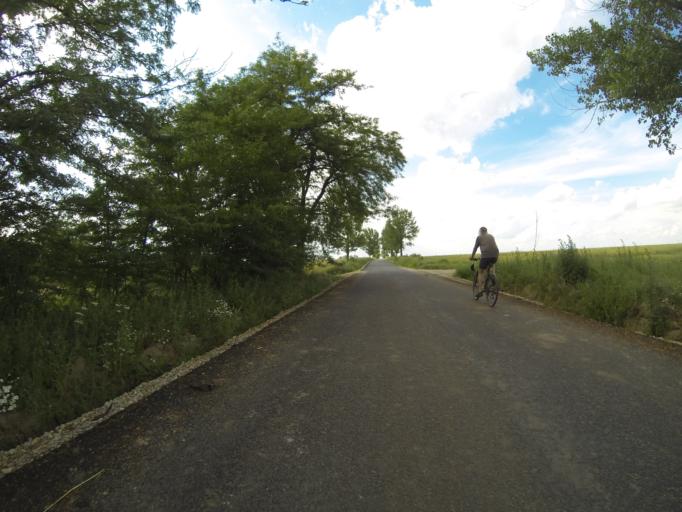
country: RO
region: Dolj
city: Satu Nou Calopar
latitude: 44.1371
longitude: 23.7952
